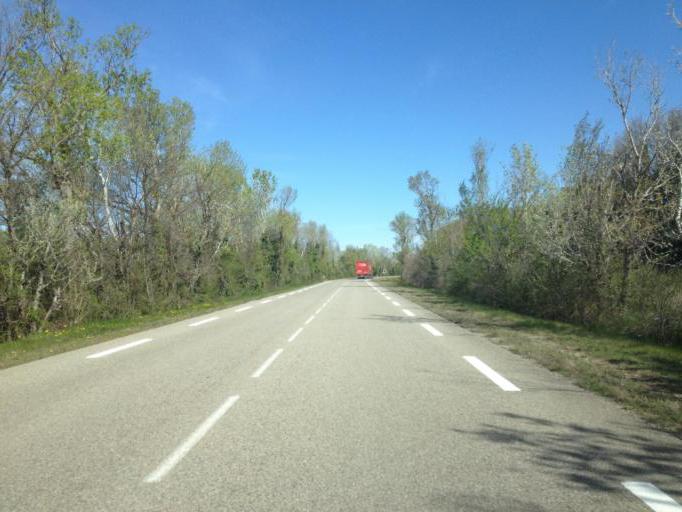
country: FR
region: Provence-Alpes-Cote d'Azur
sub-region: Departement du Vaucluse
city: Caderousse
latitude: 44.1227
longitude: 4.7191
